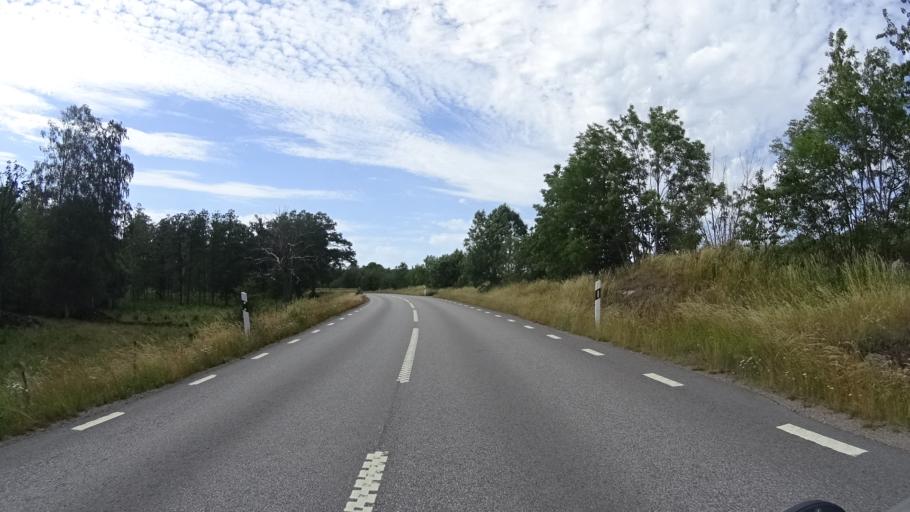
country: SE
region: OEstergoetland
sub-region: Atvidabergs Kommun
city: Atvidaberg
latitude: 58.1391
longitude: 16.0878
